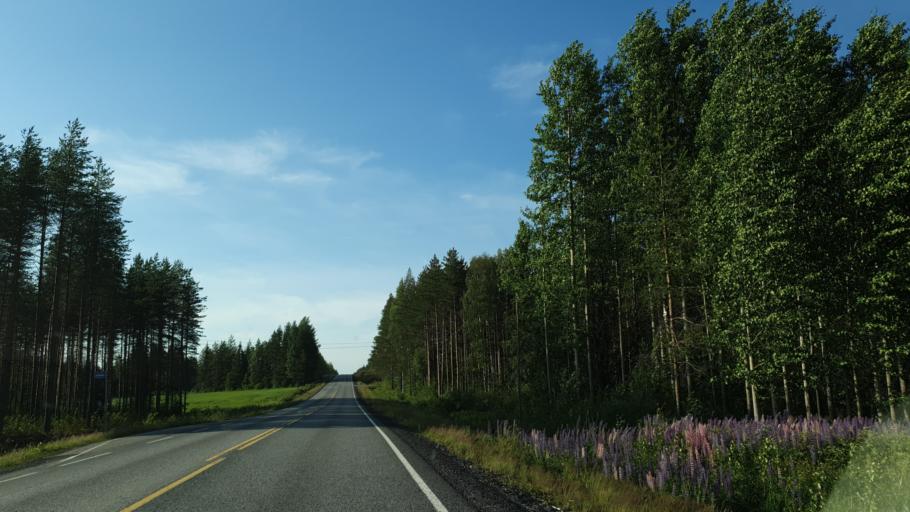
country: FI
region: Kainuu
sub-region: Kehys-Kainuu
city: Kuhmo
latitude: 64.0812
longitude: 29.4855
